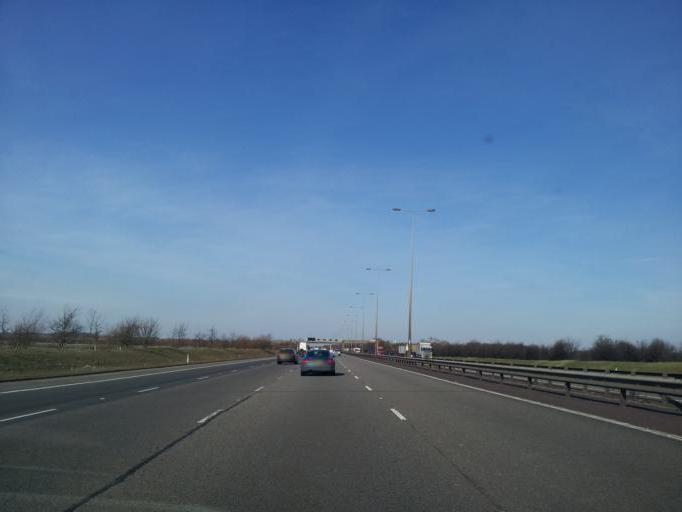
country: GB
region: England
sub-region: Cambridgeshire
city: Sawtry
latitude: 52.4609
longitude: -0.2814
